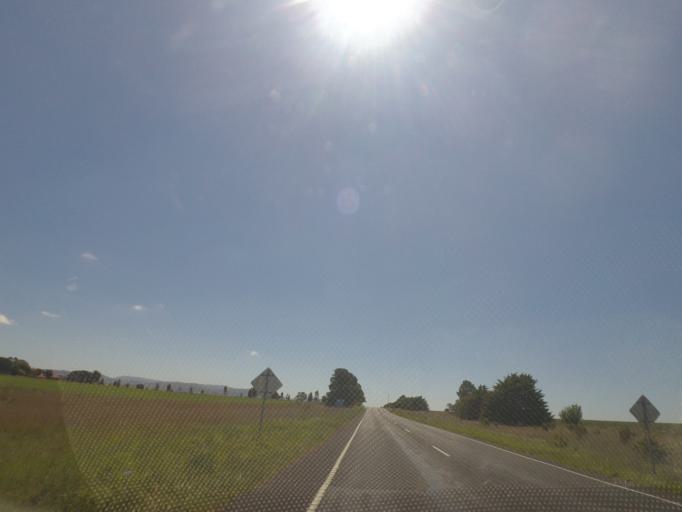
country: AU
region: Victoria
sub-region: Hume
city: Sunbury
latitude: -37.4848
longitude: 144.7536
